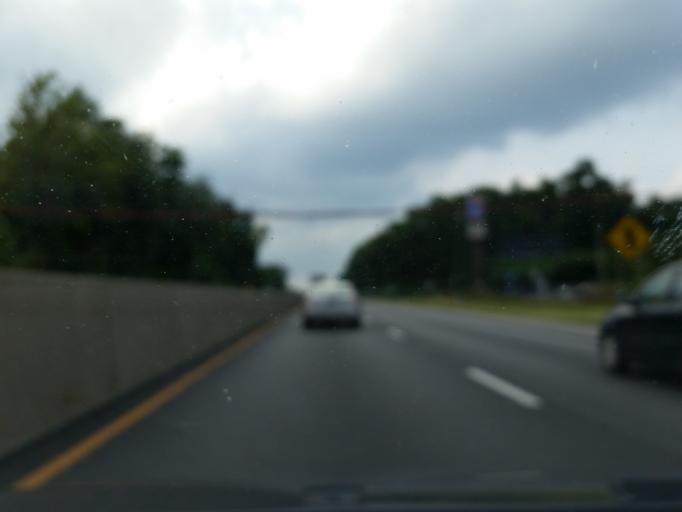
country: US
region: Pennsylvania
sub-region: York County
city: Valley Green
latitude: 40.1706
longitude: -76.8317
